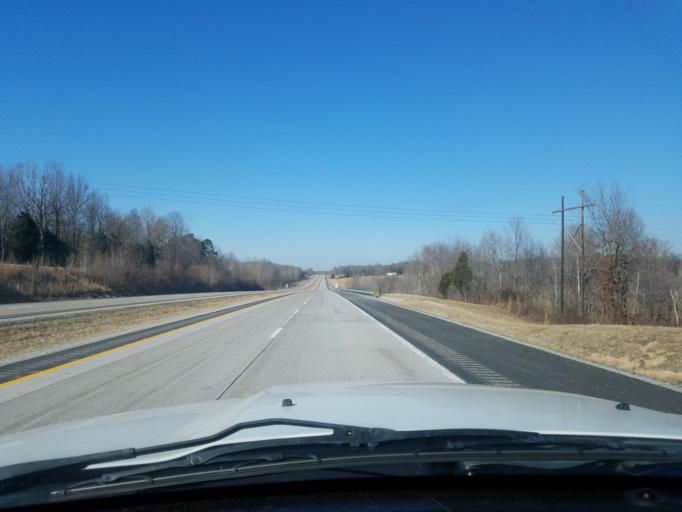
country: US
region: Kentucky
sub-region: Ohio County
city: Beaver Dam
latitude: 37.3994
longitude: -86.8195
